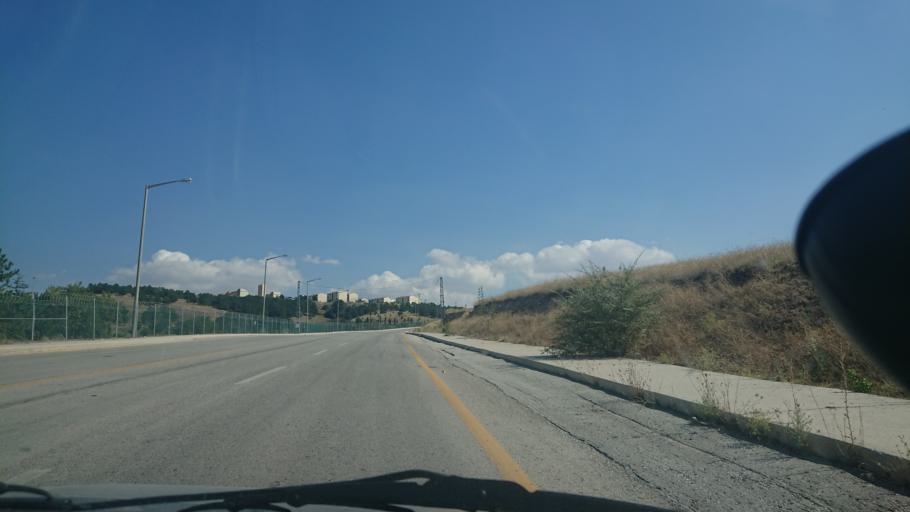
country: TR
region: Ankara
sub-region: Goelbasi
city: Golbasi
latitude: 39.8058
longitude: 32.8291
